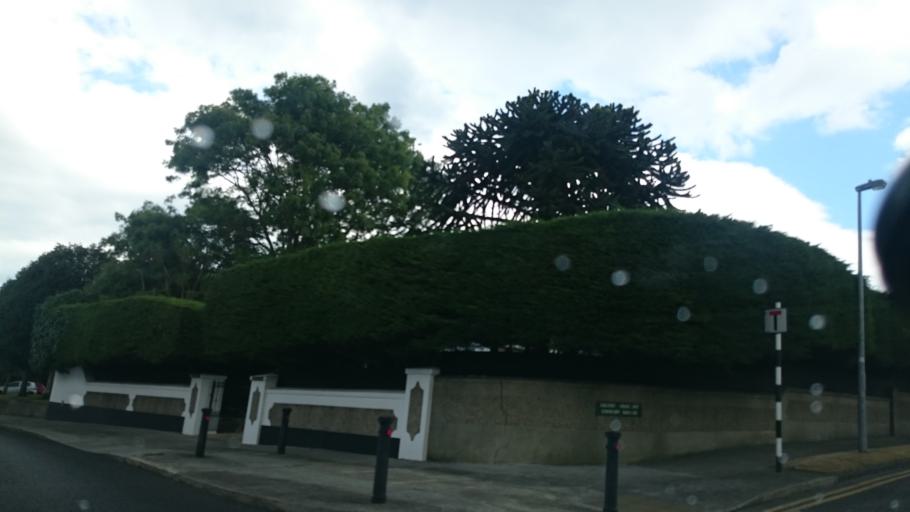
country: IE
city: Booterstown
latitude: 53.3010
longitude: -6.2008
